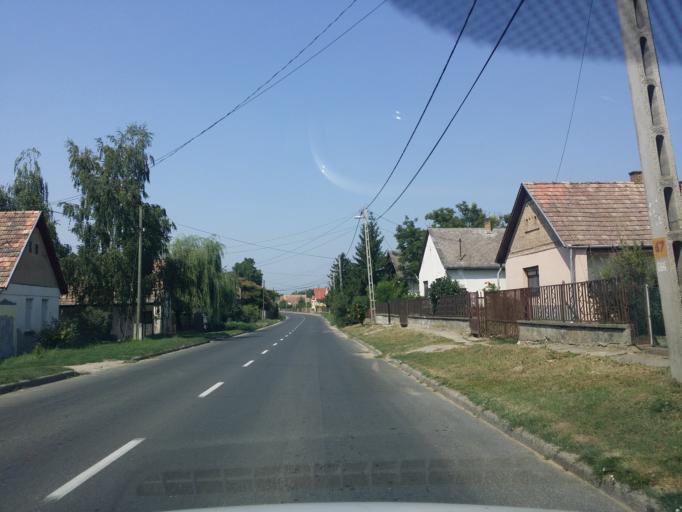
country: HU
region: Tolna
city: Pincehely
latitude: 46.7089
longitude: 18.4713
